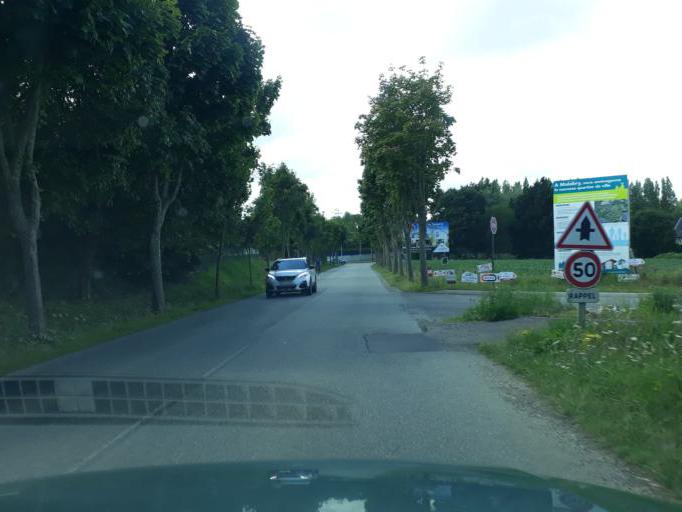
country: FR
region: Brittany
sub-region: Departement des Cotes-d'Armor
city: Paimpol
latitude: 48.7679
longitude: -3.0356
